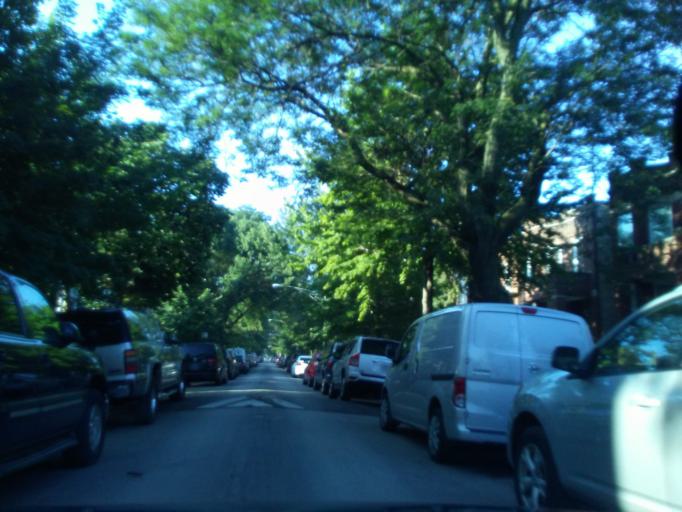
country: US
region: Illinois
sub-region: Cook County
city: Lincolnwood
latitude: 41.9350
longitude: -87.7246
